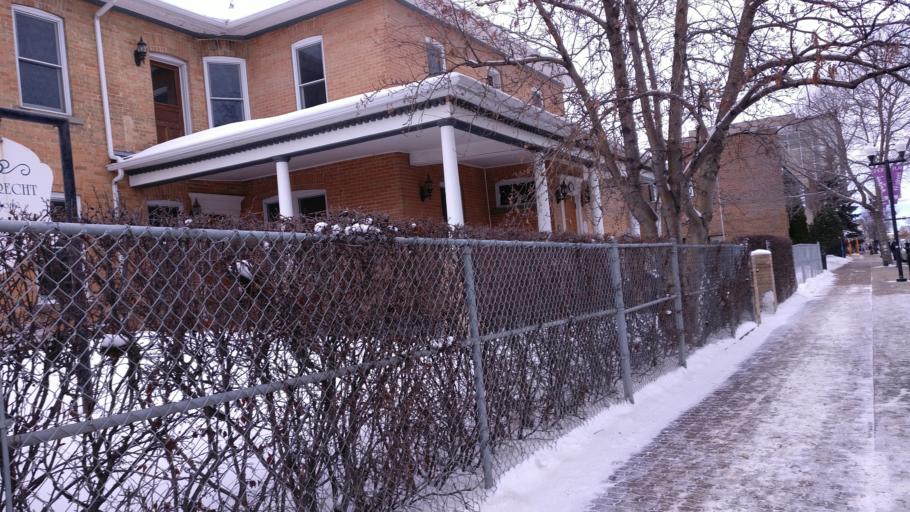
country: CA
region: Alberta
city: Red Deer
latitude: 52.2680
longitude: -113.8091
